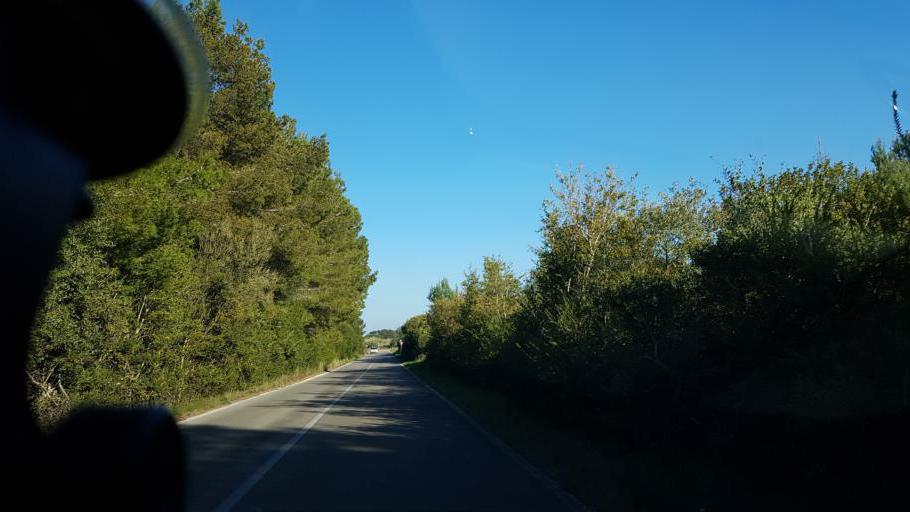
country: IT
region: Apulia
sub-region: Provincia di Lecce
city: Struda
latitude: 40.3896
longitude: 18.2916
